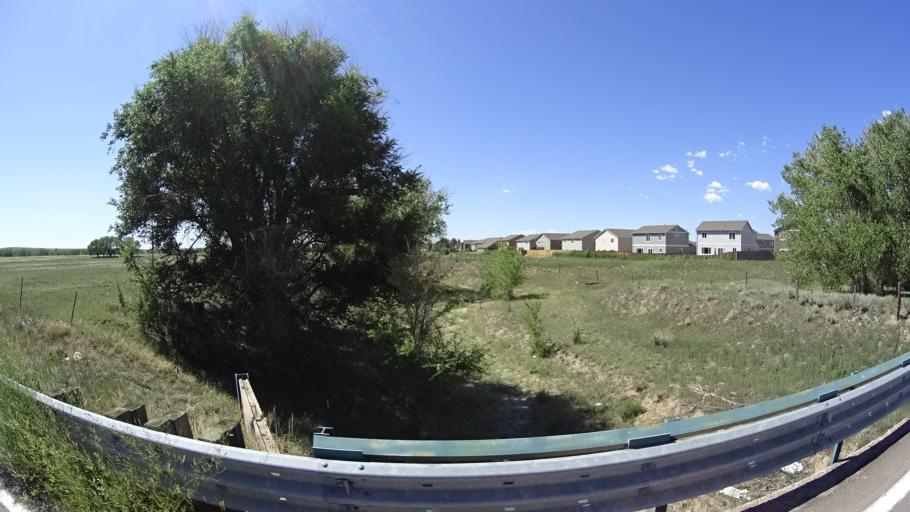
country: US
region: Colorado
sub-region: El Paso County
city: Security-Widefield
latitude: 38.7810
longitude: -104.6507
